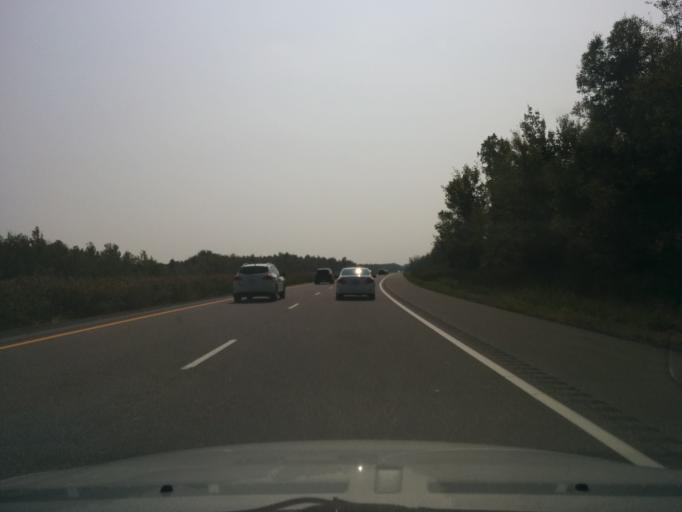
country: CA
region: Ontario
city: Bells Corners
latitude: 45.0792
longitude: -75.6305
